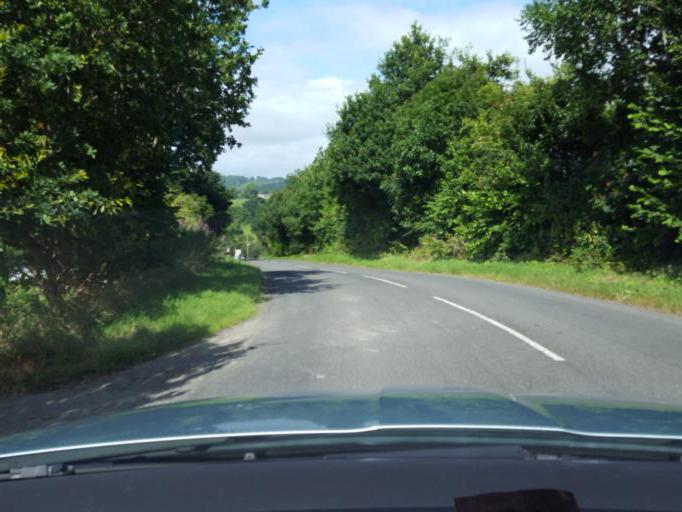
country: GB
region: Wales
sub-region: Denbighshire
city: Corwen
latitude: 52.9858
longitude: -3.3654
